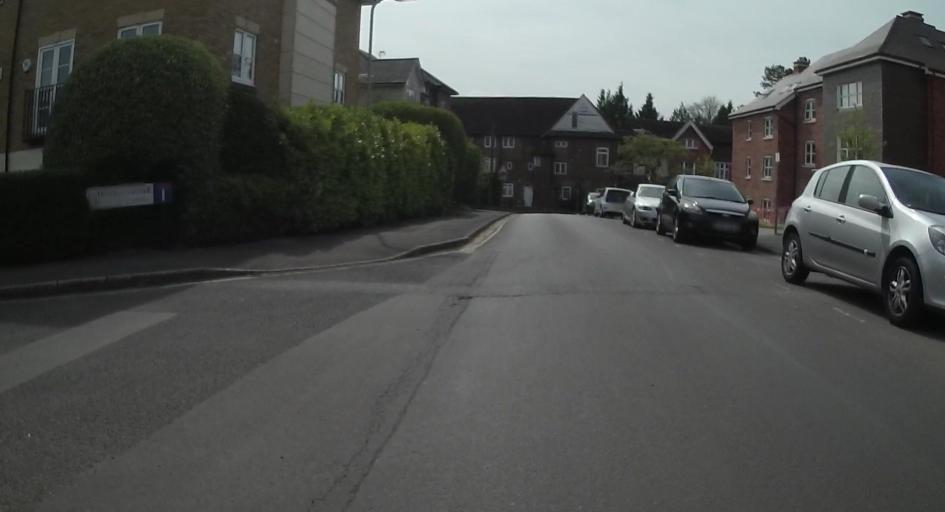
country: GB
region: England
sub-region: Hampshire
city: Winchester
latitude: 51.0621
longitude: -1.3354
